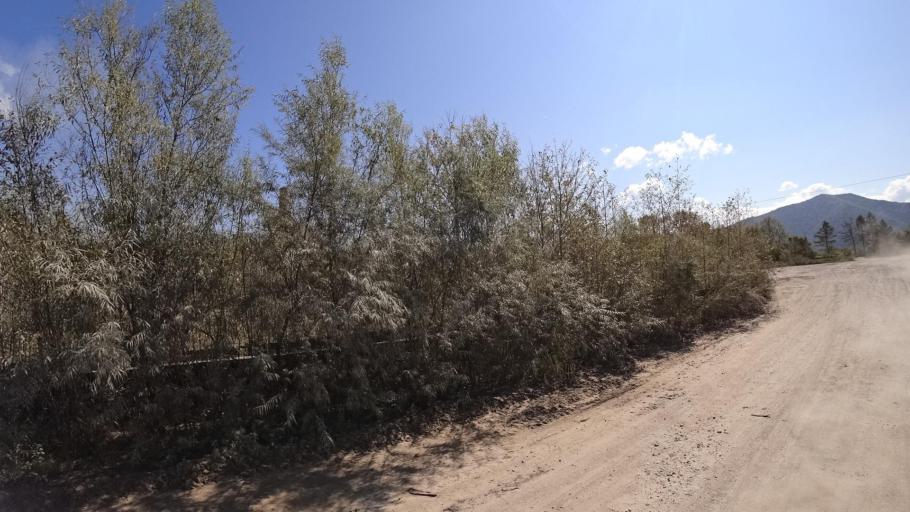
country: RU
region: Jewish Autonomous Oblast
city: Londoko
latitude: 49.0033
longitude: 131.8876
